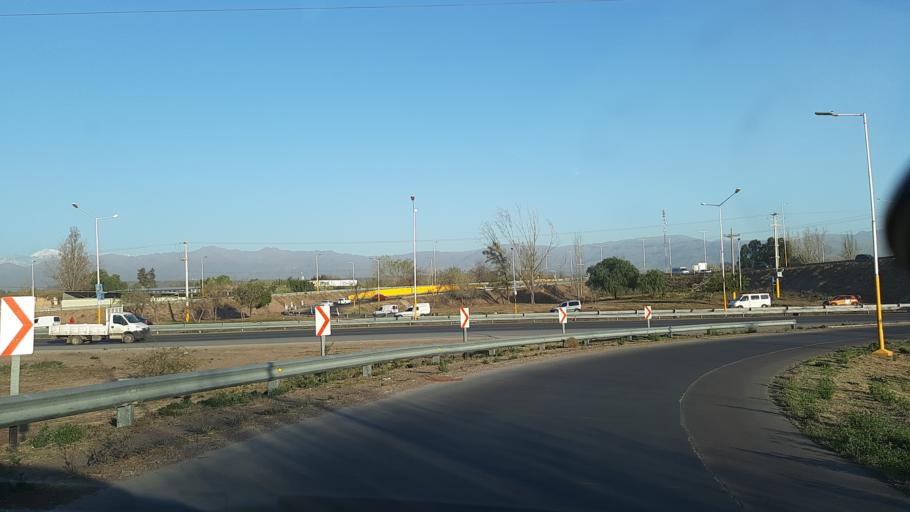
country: AR
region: Mendoza
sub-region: Departamento de Godoy Cruz
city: Godoy Cruz
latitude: -32.9689
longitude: -68.8415
